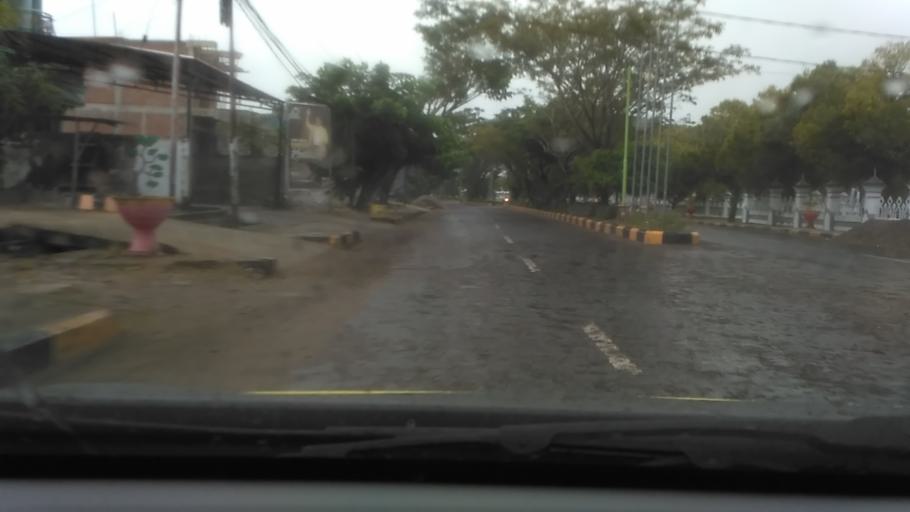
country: ID
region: South Sulawesi
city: Pinrang
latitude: -3.8109
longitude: 119.6502
